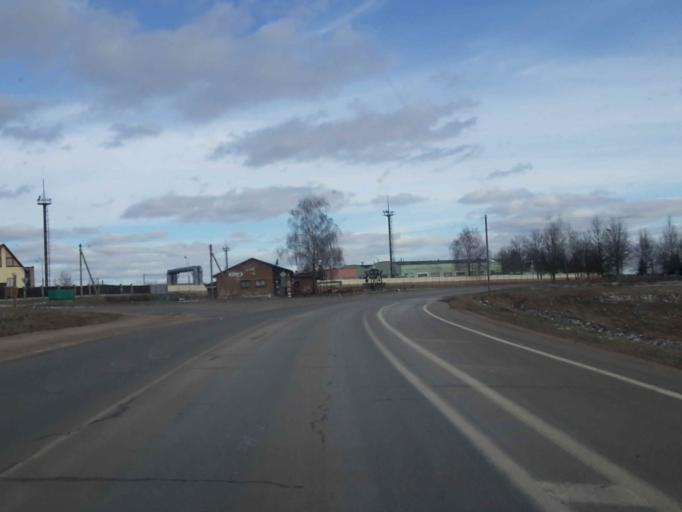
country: BY
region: Minsk
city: Myadzyel
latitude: 54.8855
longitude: 26.9349
